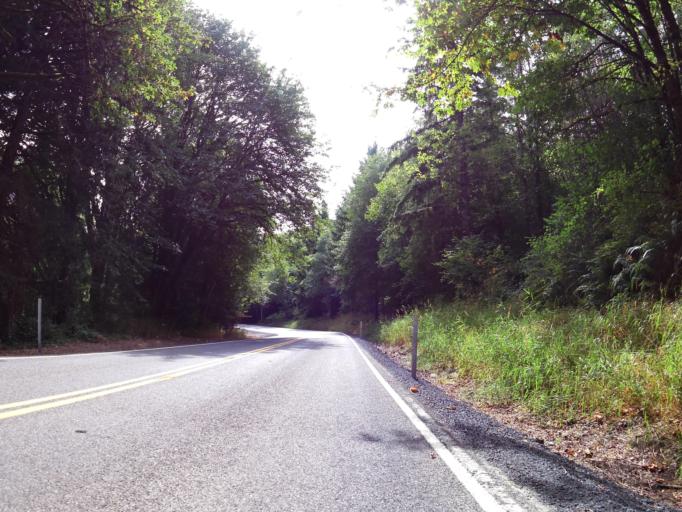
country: US
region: Washington
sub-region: Lewis County
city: Napavine
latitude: 46.5535
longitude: -122.9578
